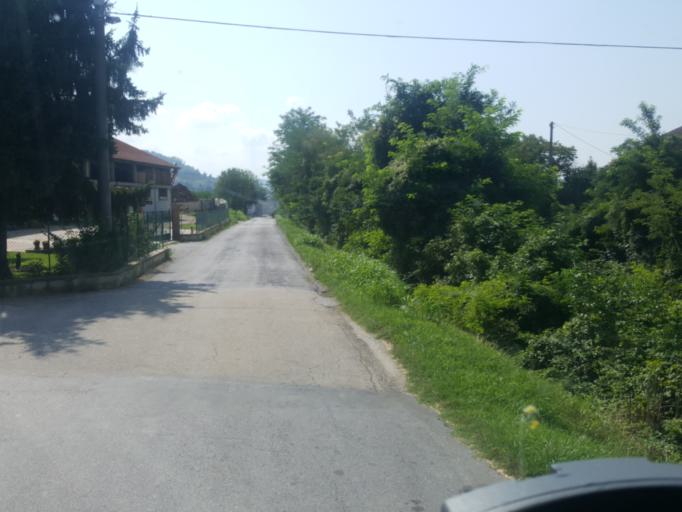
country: IT
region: Piedmont
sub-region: Provincia di Cuneo
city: Narzole
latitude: 44.5969
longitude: 7.8939
